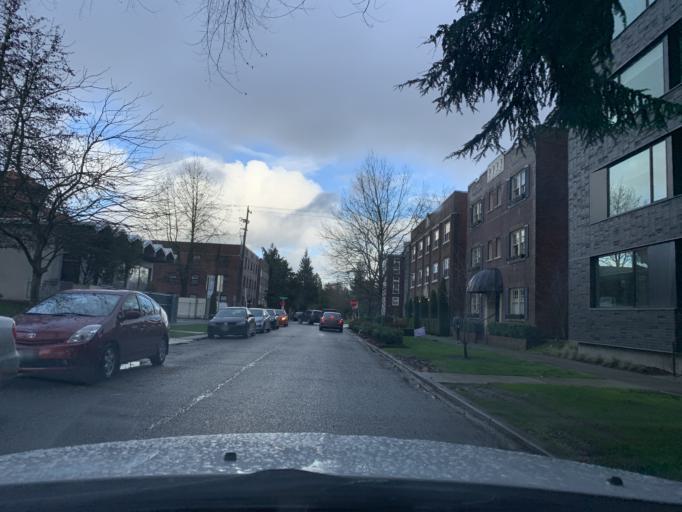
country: US
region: Washington
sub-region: King County
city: Seattle
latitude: 47.6199
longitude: -122.3114
